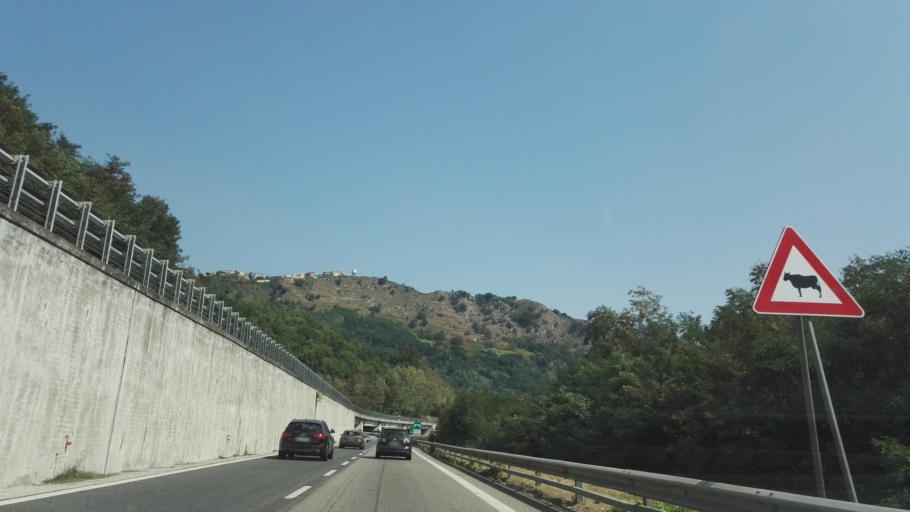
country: IT
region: Calabria
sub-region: Provincia di Cosenza
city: Altilia
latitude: 39.1157
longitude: 16.2554
